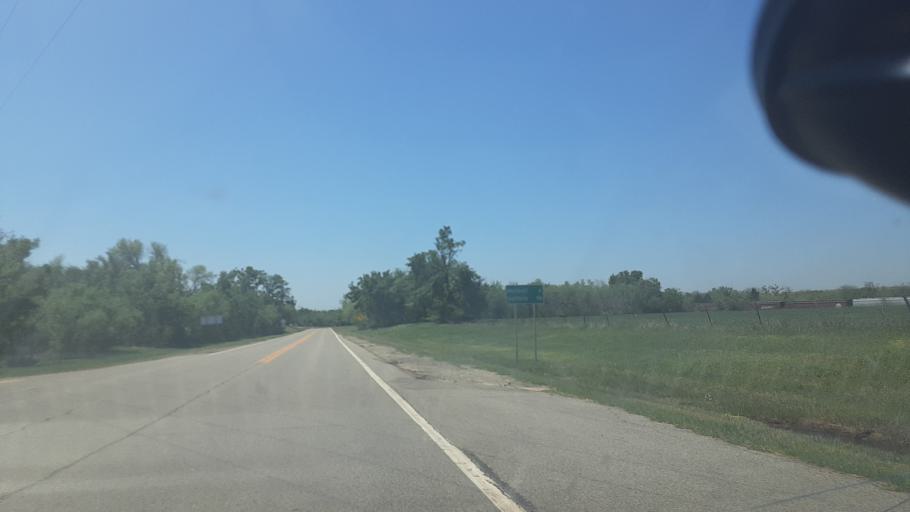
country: US
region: Oklahoma
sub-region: Noble County
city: Perry
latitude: 36.1095
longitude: -97.3897
